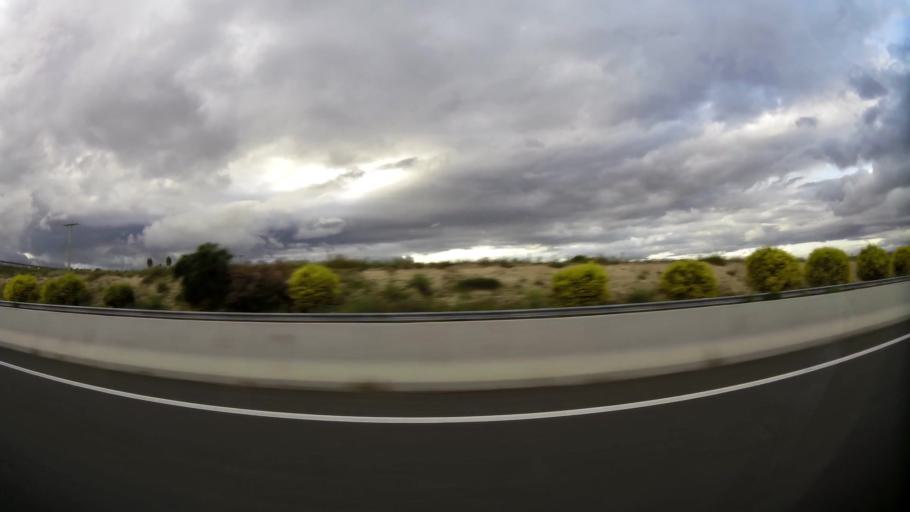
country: MA
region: Taza-Al Hoceima-Taounate
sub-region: Taza
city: Taza
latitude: 34.2531
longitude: -3.8913
